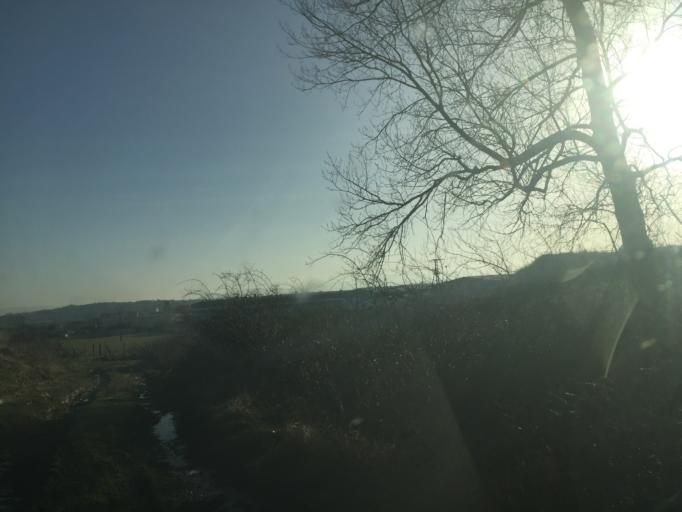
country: ES
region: Castille and Leon
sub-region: Provincia de Burgos
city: Medina de Pomar
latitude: 42.9251
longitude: -3.5866
